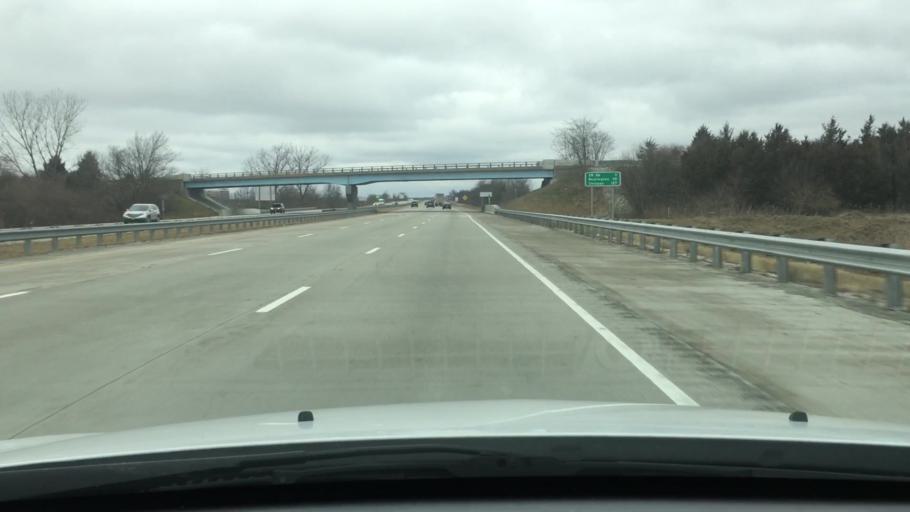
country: US
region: Indiana
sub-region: Tippecanoe County
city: Dayton
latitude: 40.3875
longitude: -86.7893
